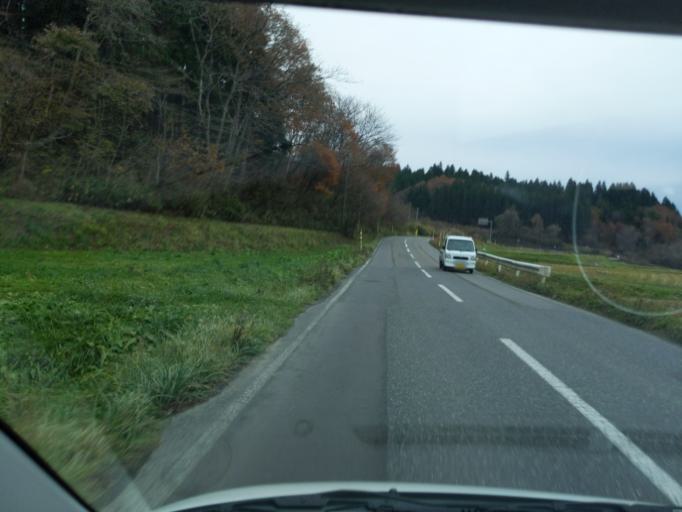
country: JP
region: Iwate
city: Kitakami
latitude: 39.2640
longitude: 141.2684
